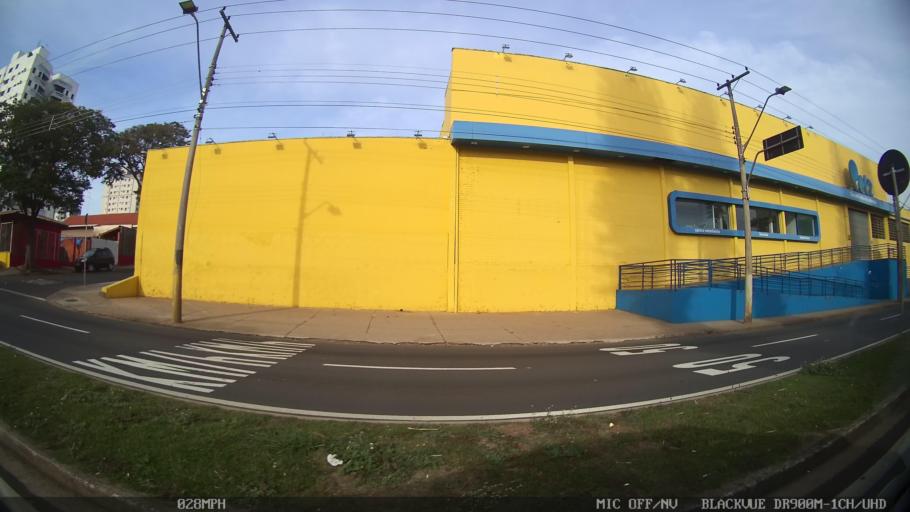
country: BR
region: Sao Paulo
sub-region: Piracicaba
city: Piracicaba
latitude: -22.7106
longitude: -47.6399
